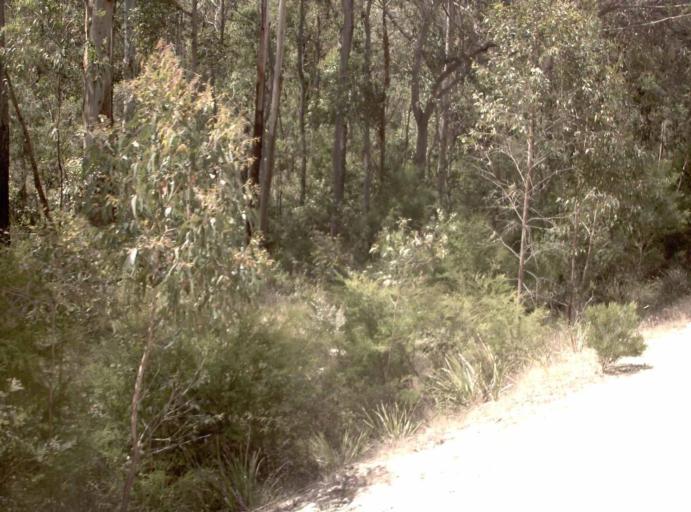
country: AU
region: New South Wales
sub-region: Bombala
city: Bombala
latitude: -37.5678
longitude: 149.2188
